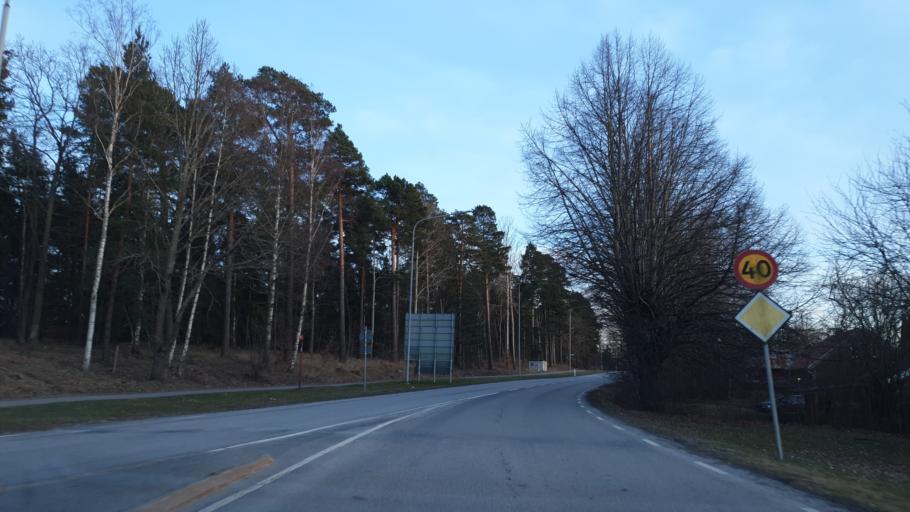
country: SE
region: Uppsala
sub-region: Habo Kommun
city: Balsta
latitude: 59.5590
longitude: 17.5445
